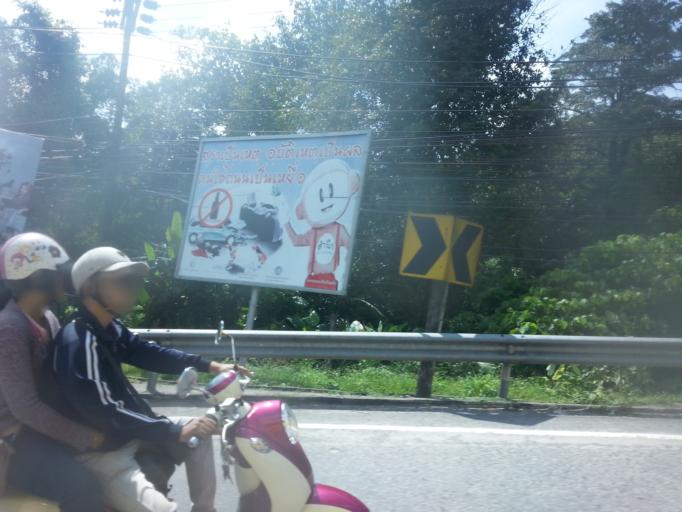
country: TH
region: Phuket
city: Kathu
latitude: 7.9045
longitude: 98.3242
